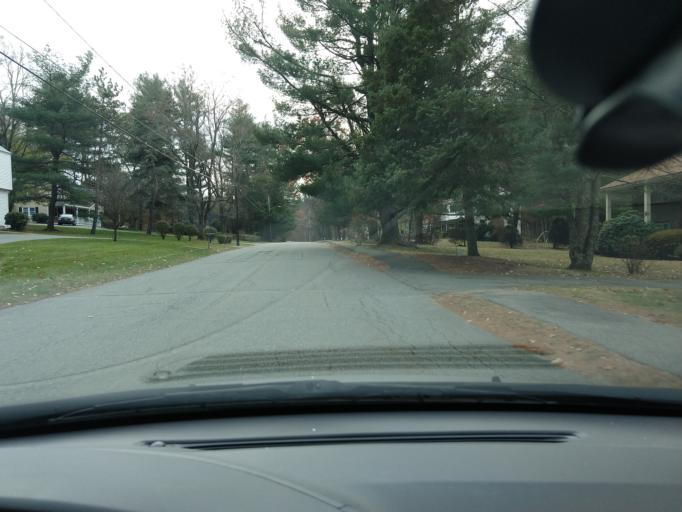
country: US
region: Massachusetts
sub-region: Middlesex County
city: Bedford
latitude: 42.5038
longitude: -71.2505
